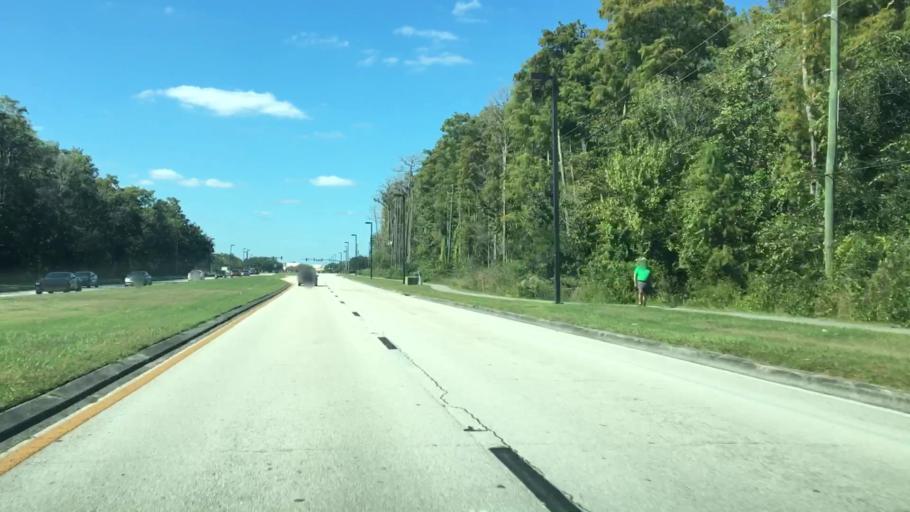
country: US
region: Florida
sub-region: Orange County
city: Conway
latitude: 28.4662
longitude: -81.2931
